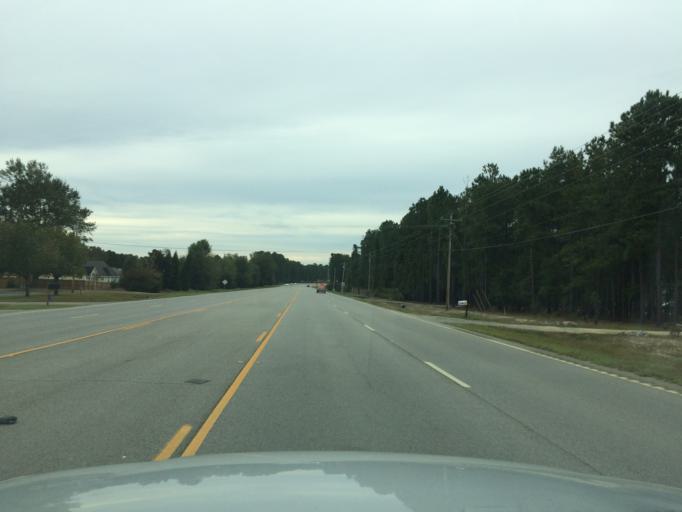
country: US
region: South Carolina
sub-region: Aiken County
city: Aiken
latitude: 33.6257
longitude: -81.6789
